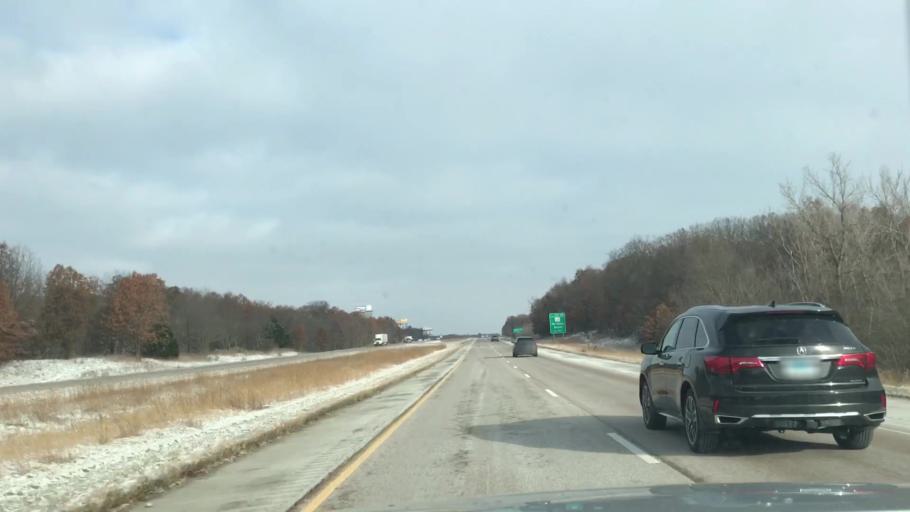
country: US
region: Illinois
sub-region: Macoupin County
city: Mount Olive
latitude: 39.0593
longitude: -89.7556
